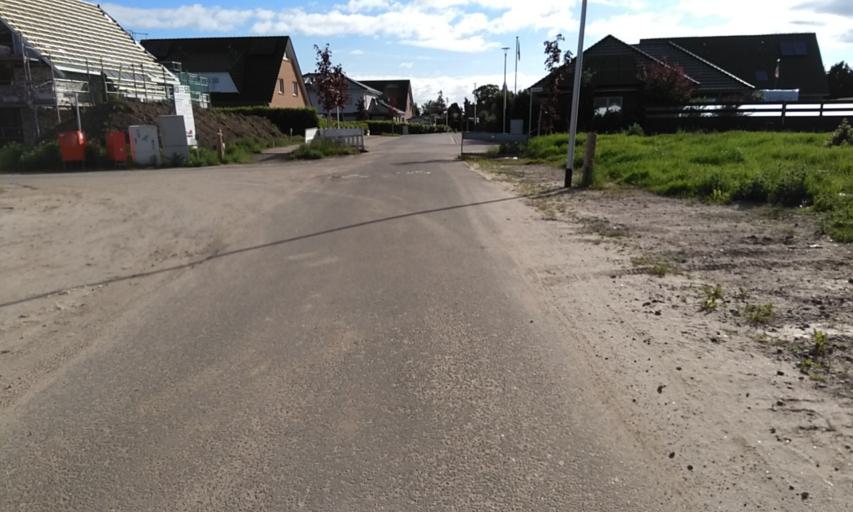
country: DE
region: Lower Saxony
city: Apensen
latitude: 53.4397
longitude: 9.6234
